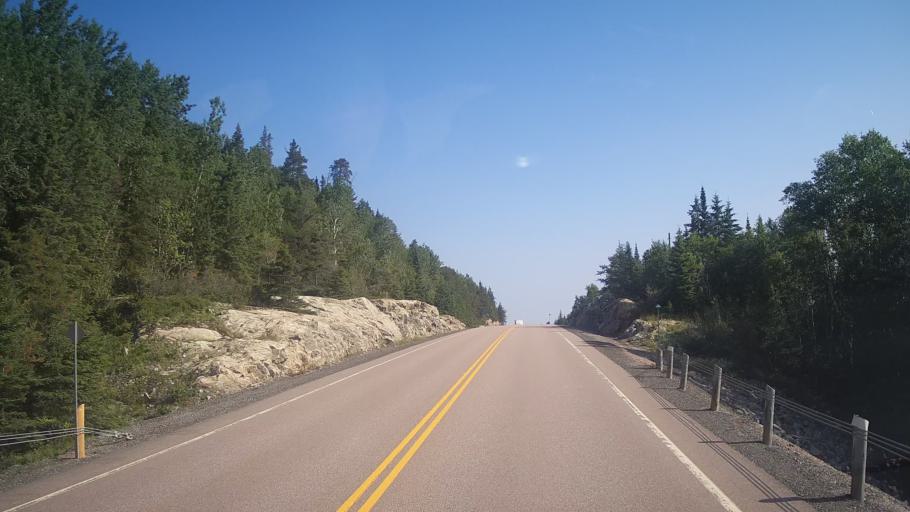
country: CA
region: Ontario
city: Rayside-Balfour
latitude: 46.9904
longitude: -81.6330
